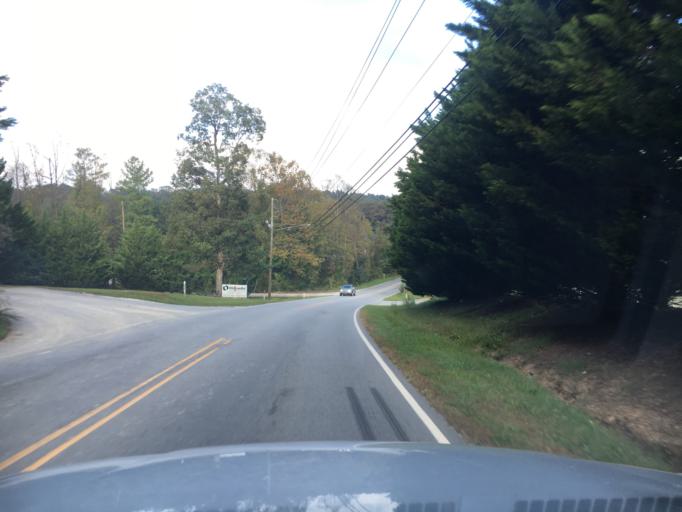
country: US
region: North Carolina
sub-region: Henderson County
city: Fletcher
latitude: 35.4334
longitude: -82.5128
